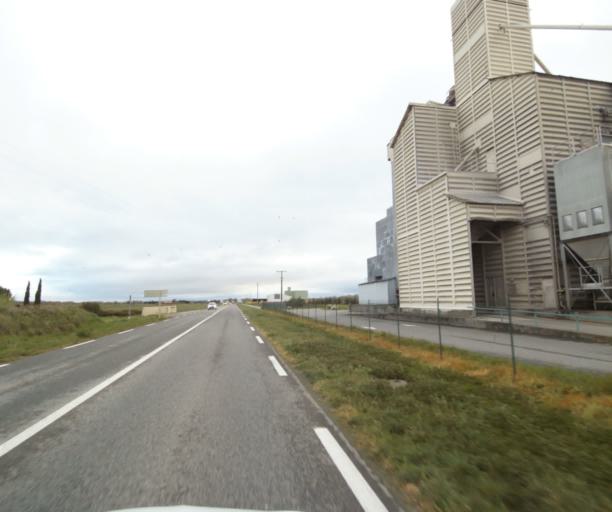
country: FR
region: Midi-Pyrenees
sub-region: Departement de l'Ariege
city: Saverdun
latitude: 43.1989
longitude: 1.6097
